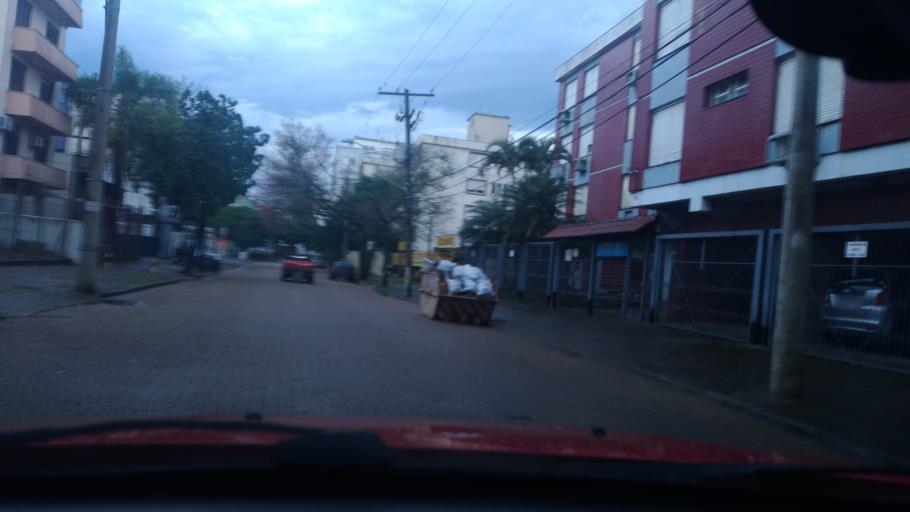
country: BR
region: Rio Grande do Sul
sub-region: Porto Alegre
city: Porto Alegre
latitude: -30.0102
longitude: -51.1639
